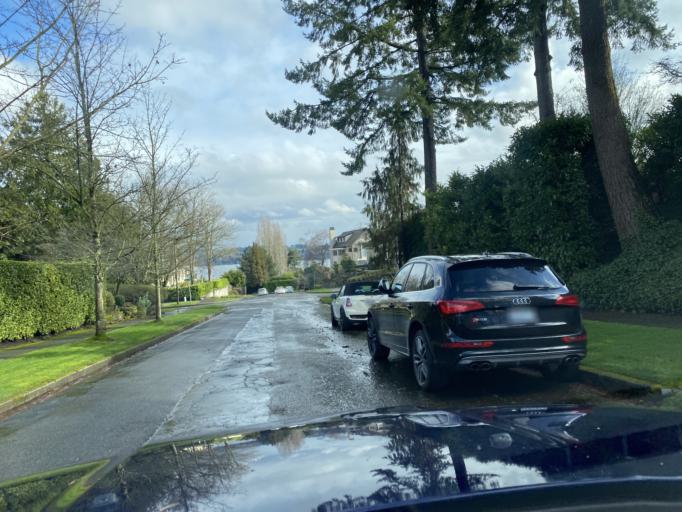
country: US
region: Washington
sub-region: King County
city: Seattle
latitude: 47.6298
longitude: -122.2849
